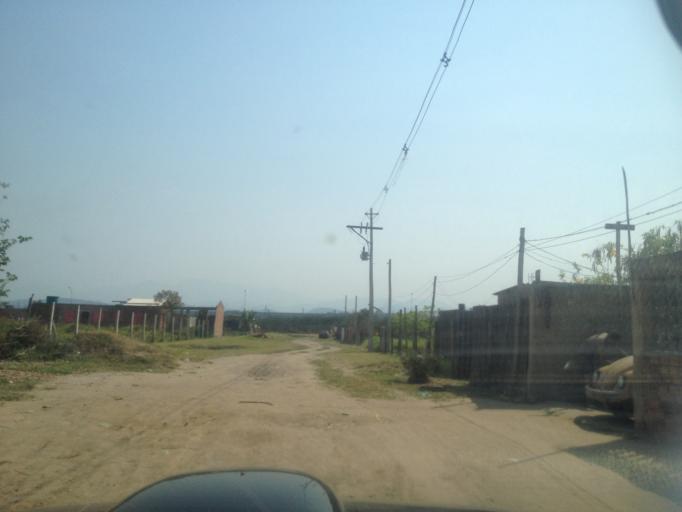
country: BR
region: Rio de Janeiro
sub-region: Porto Real
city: Porto Real
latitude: -22.4310
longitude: -44.3420
